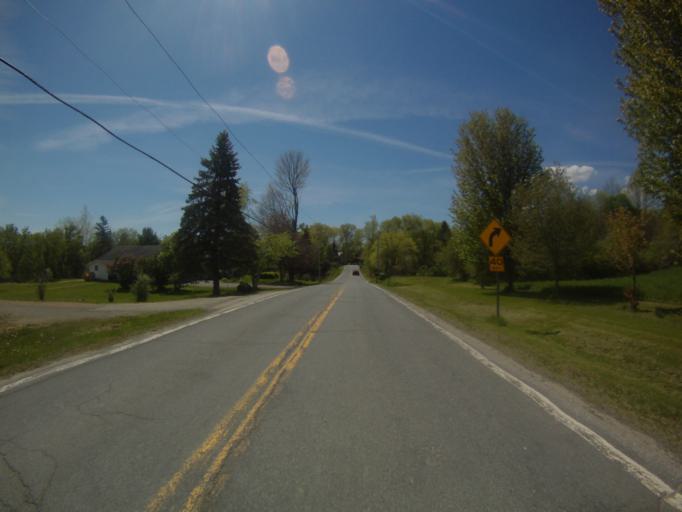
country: US
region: New York
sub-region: Essex County
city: Port Henry
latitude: 43.9669
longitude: -73.4208
